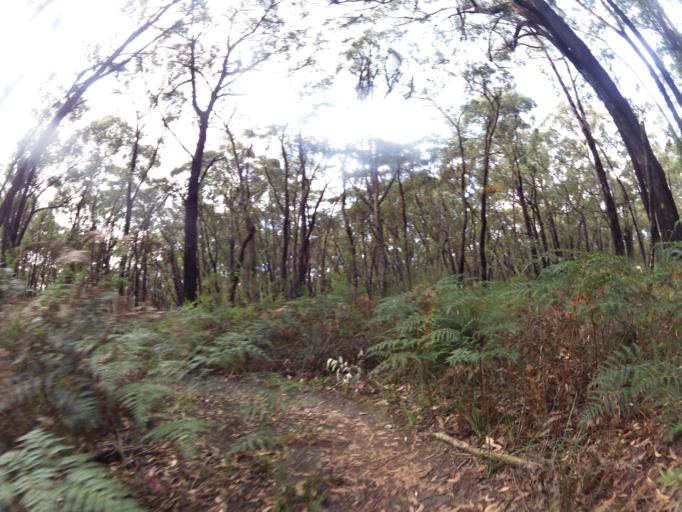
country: AU
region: Victoria
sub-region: Colac-Otway
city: Colac
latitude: -38.4969
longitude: 143.7121
